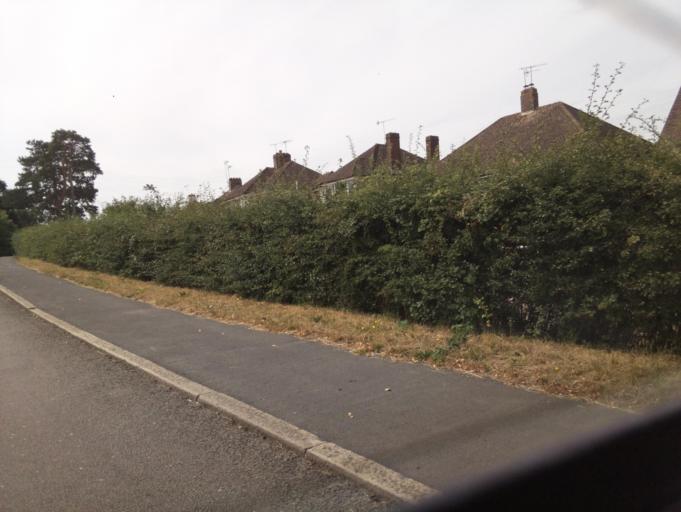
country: GB
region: England
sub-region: Surrey
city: Reigate
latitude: 51.2225
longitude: -0.1991
